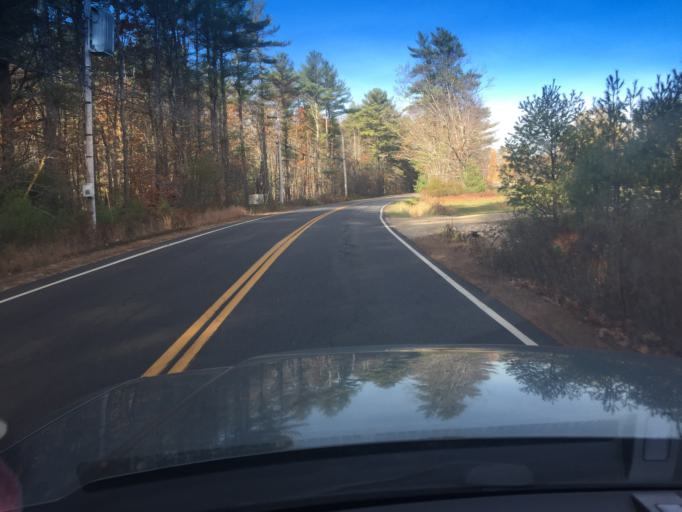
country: US
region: Maine
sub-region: York County
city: Eliot
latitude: 43.1754
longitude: -70.7234
